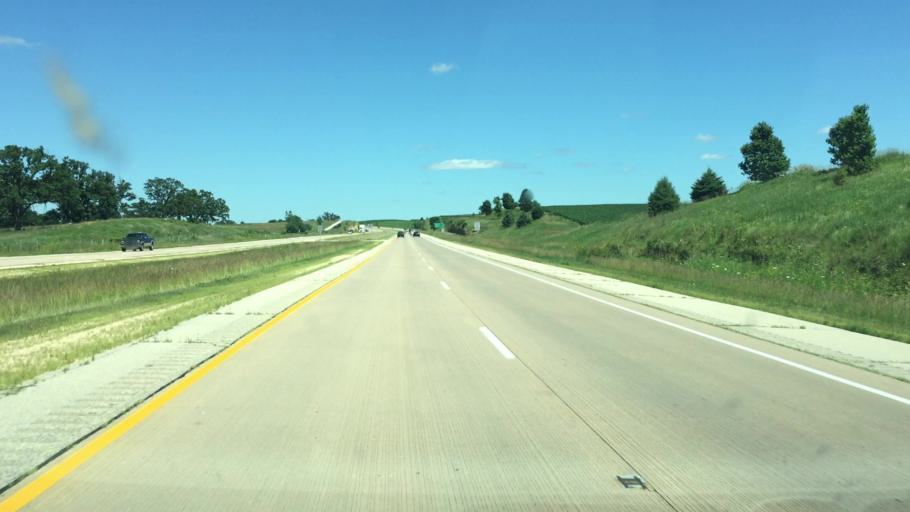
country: US
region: Wisconsin
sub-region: Grant County
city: Platteville
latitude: 42.7372
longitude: -90.4232
